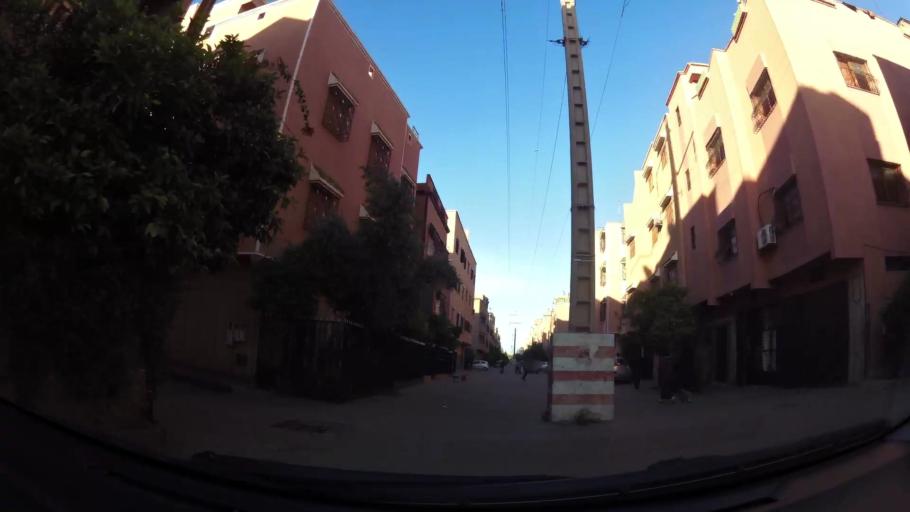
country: MA
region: Marrakech-Tensift-Al Haouz
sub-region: Marrakech
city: Marrakesh
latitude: 31.6203
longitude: -8.0502
